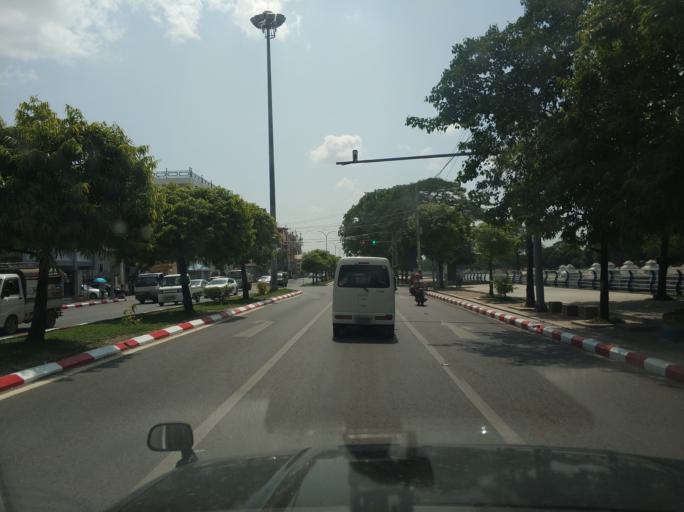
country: MM
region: Mandalay
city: Mandalay
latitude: 21.9825
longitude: 96.0965
